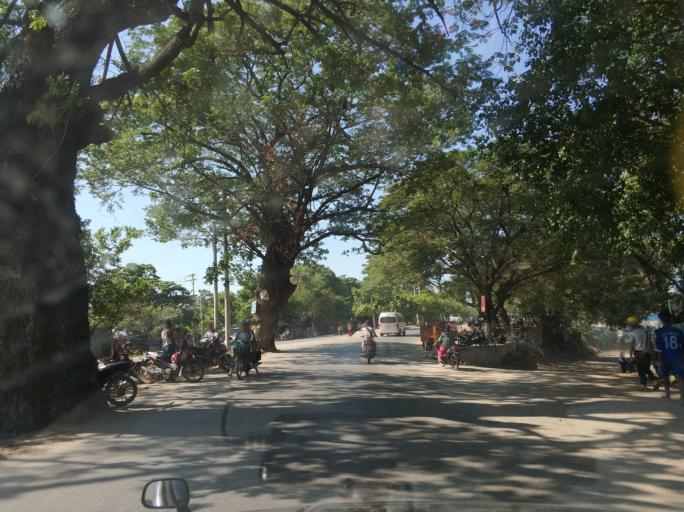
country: MM
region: Mandalay
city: Mandalay
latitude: 21.9688
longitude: 96.0563
